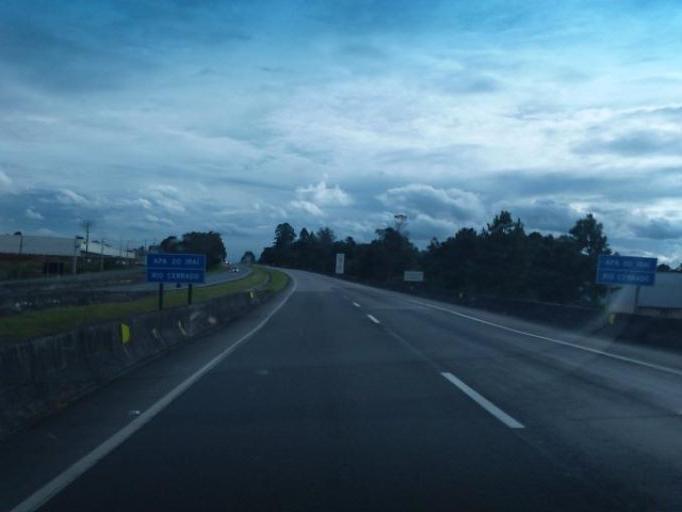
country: BR
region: Parana
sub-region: Quatro Barras
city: Quatro Barras
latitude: -25.3816
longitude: -49.0521
